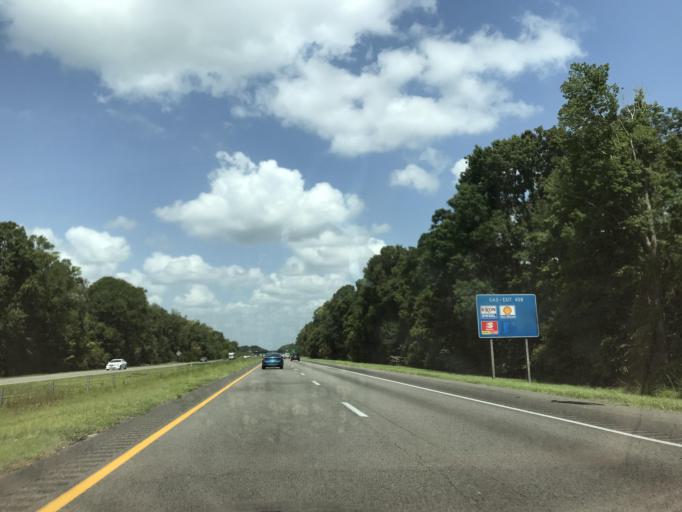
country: US
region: North Carolina
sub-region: Pender County
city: Rocky Point
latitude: 34.4316
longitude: -77.8716
